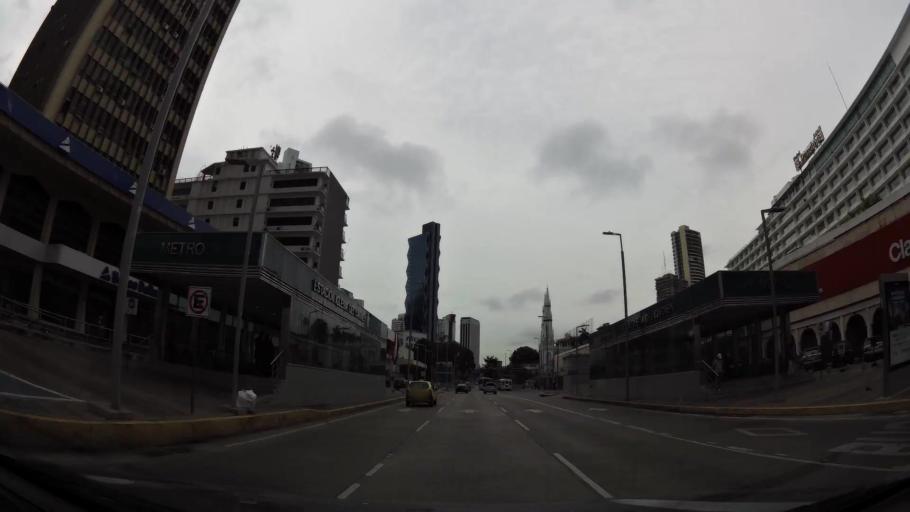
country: PA
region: Panama
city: Panama
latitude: 8.9830
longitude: -79.5266
